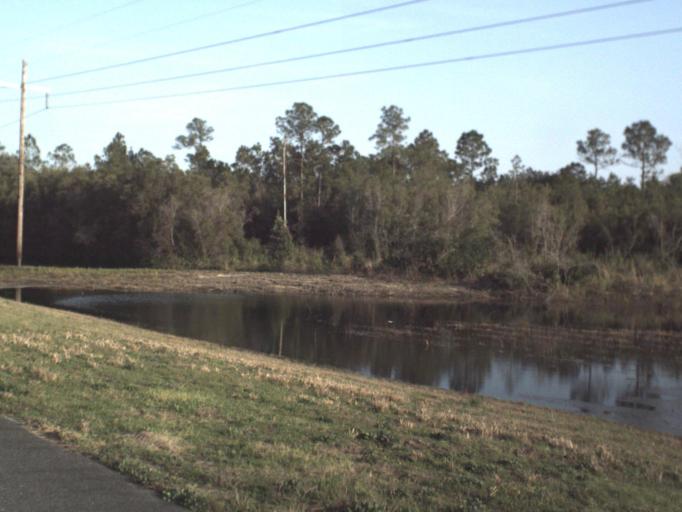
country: US
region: Florida
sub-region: Bay County
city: Laguna Beach
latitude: 30.4399
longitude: -85.8113
